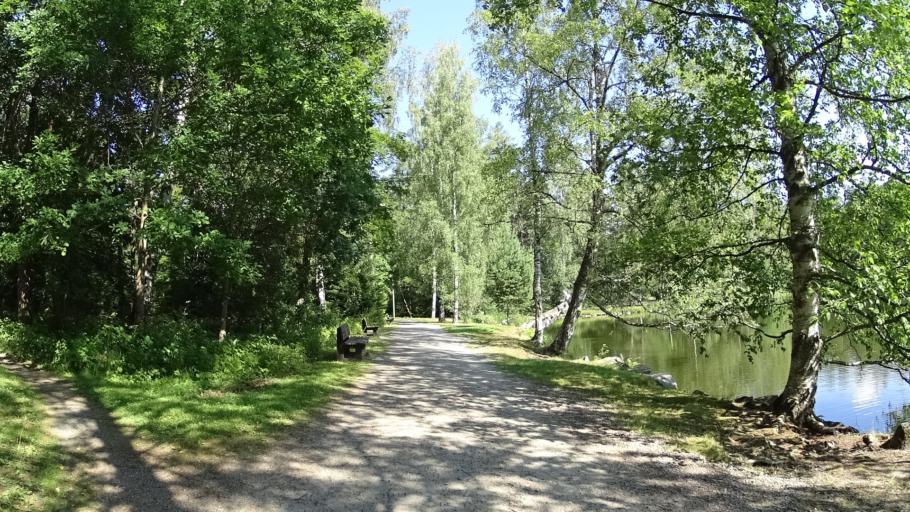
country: FI
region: Haeme
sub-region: Haemeenlinna
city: Haemeenlinna
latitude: 61.0227
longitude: 24.4545
